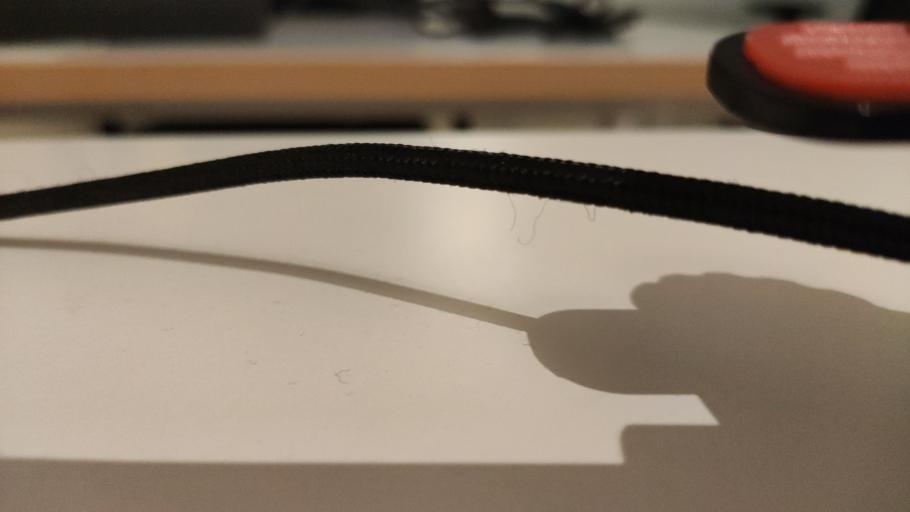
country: RU
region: Moskovskaya
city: Il'inskiy Pogost
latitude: 55.5128
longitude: 38.8714
